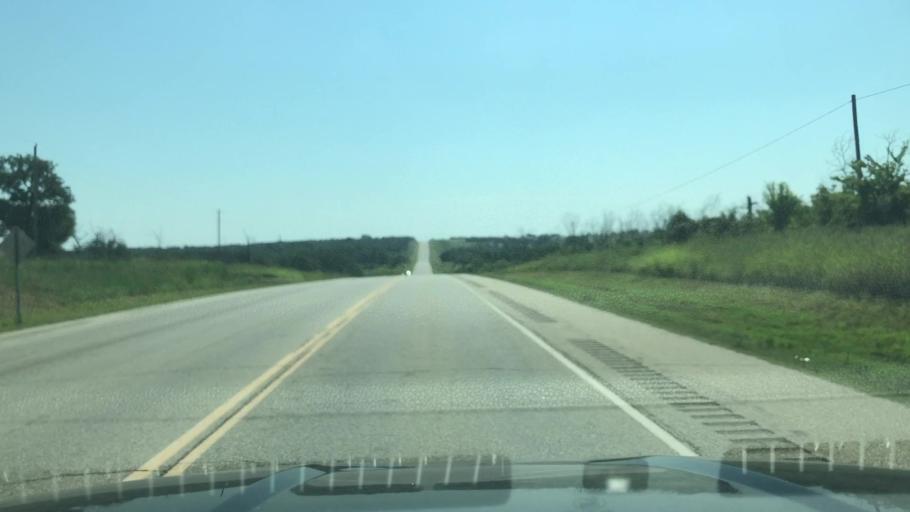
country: US
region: Oklahoma
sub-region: Creek County
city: Mannford
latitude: 36.0031
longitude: -96.4334
